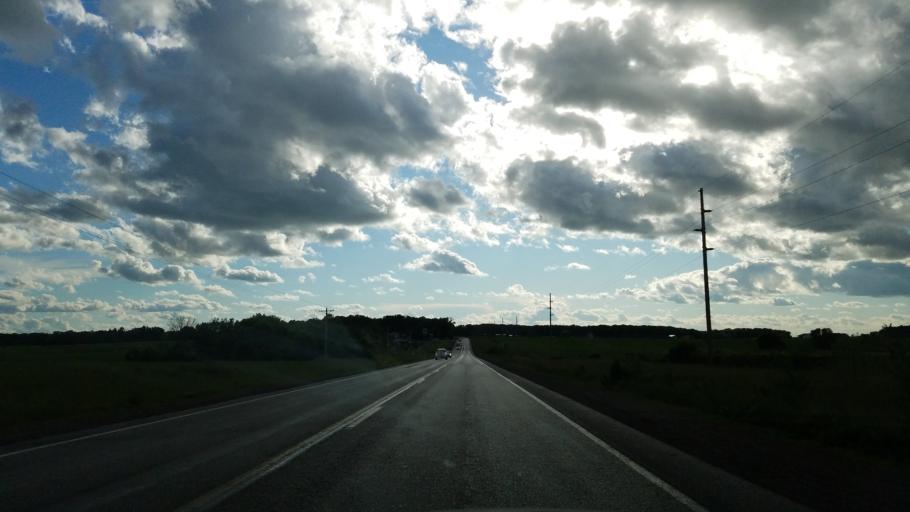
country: US
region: Wisconsin
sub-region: Polk County
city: Osceola
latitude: 45.3433
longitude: -92.6539
